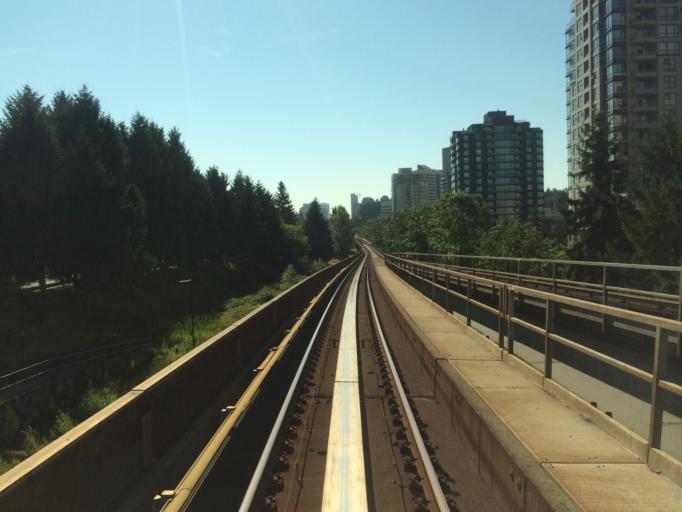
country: CA
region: British Columbia
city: Burnaby
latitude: 49.2377
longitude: -123.0301
